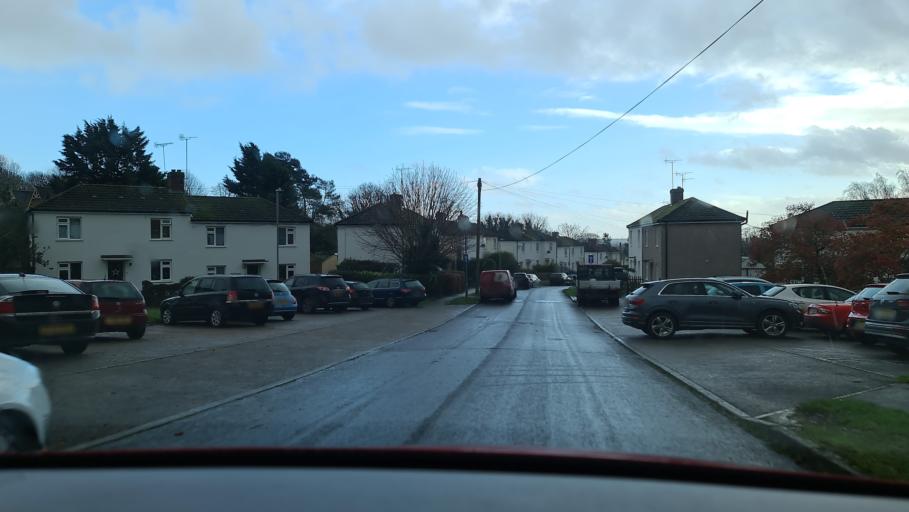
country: GB
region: England
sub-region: Buckinghamshire
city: Buckingham
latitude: 52.0039
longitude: -0.9851
